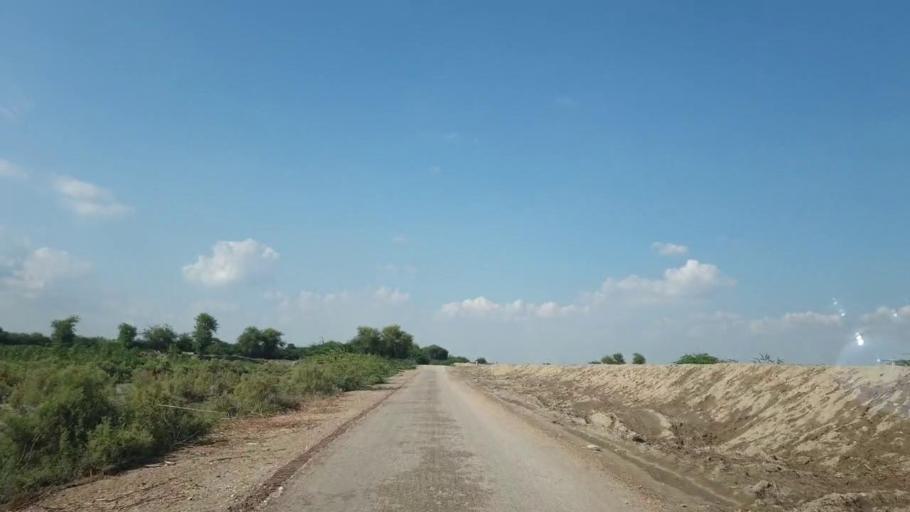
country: PK
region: Sindh
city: Pithoro
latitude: 25.6329
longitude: 69.4364
